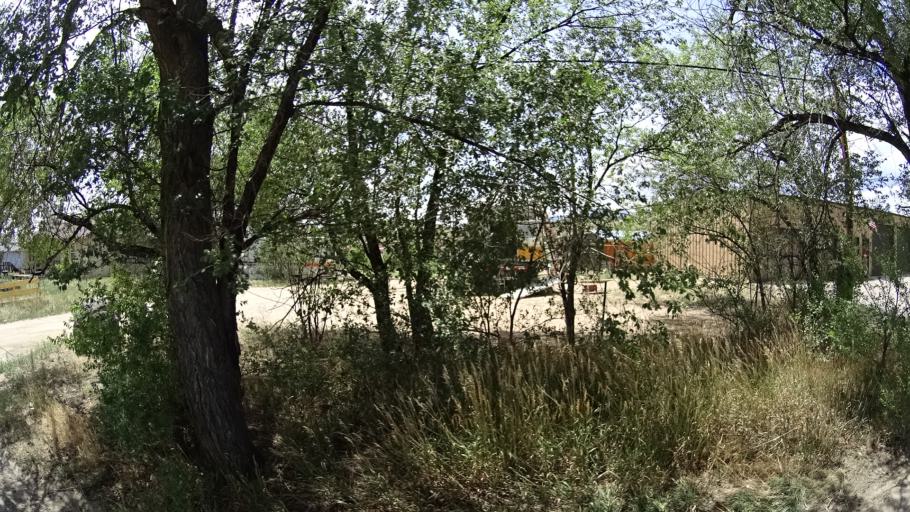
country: US
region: Colorado
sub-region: El Paso County
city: Security-Widefield
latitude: 38.7343
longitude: -104.7333
